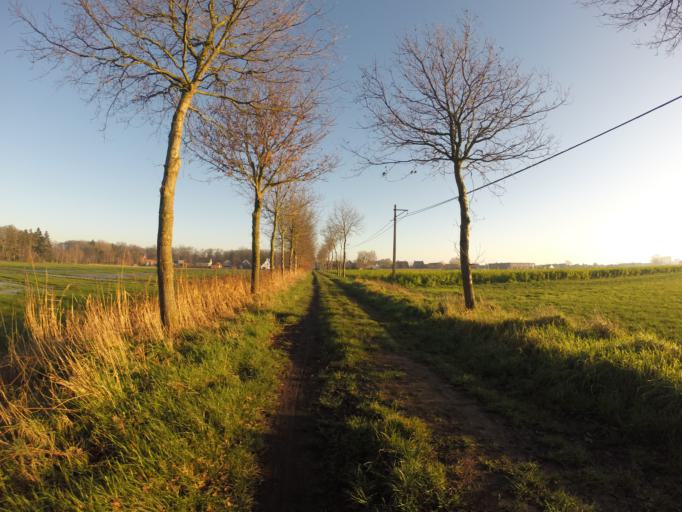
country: BE
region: Flanders
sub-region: Provincie West-Vlaanderen
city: Wingene
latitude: 51.0858
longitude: 3.3014
